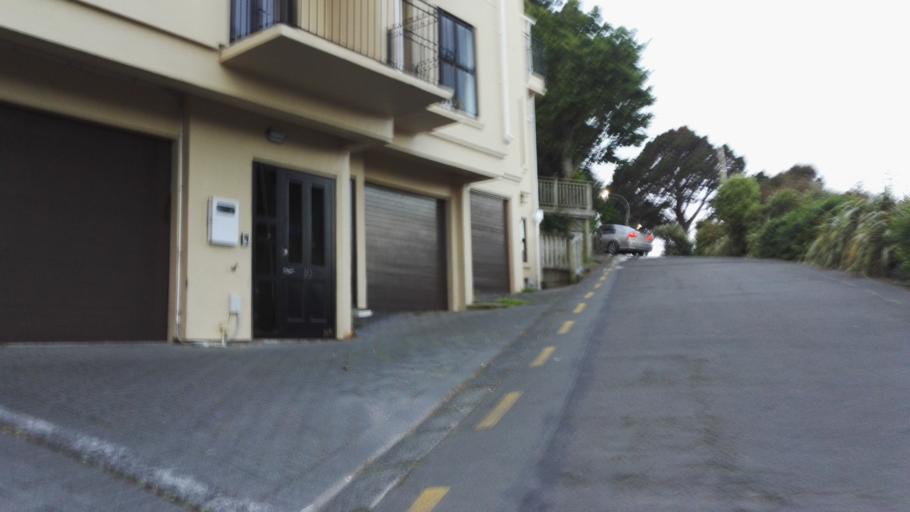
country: NZ
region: Wellington
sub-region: Wellington City
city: Wellington
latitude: -41.2938
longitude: 174.7693
